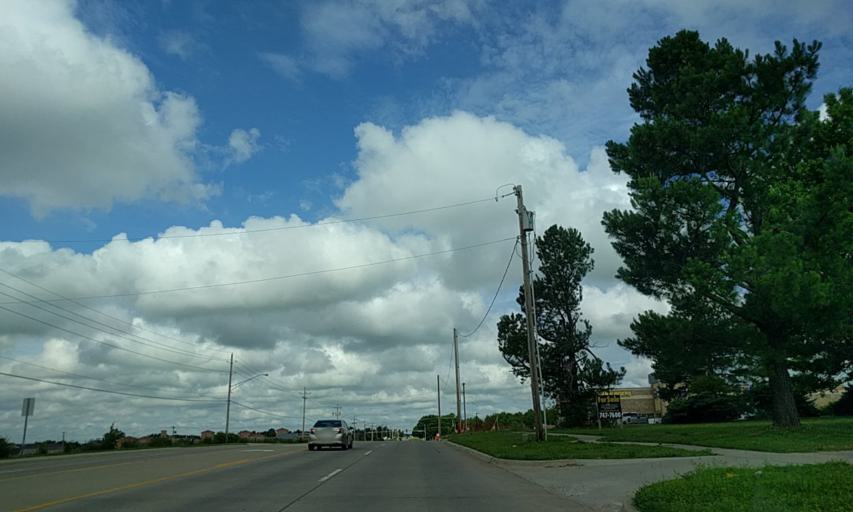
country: US
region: Oklahoma
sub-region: Tulsa County
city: Owasso
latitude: 36.2931
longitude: -95.8449
